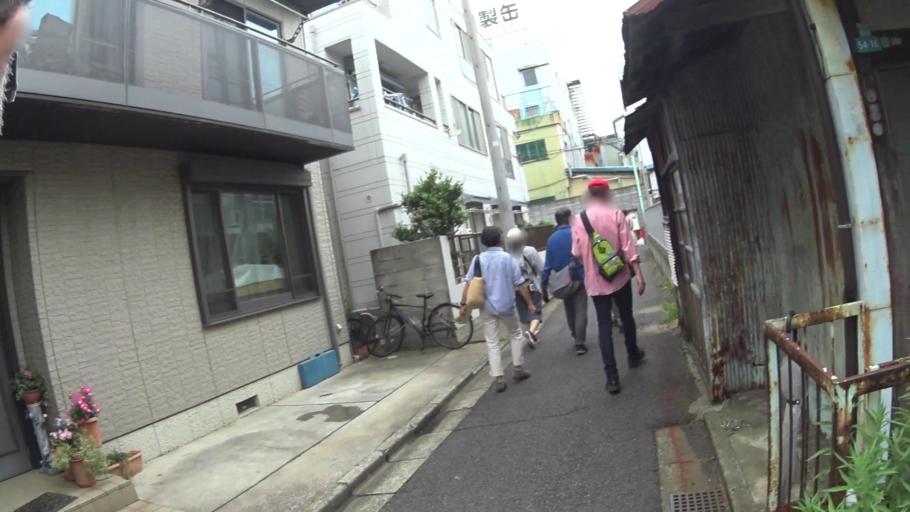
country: JP
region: Tokyo
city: Urayasu
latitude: 35.7101
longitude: 139.8462
